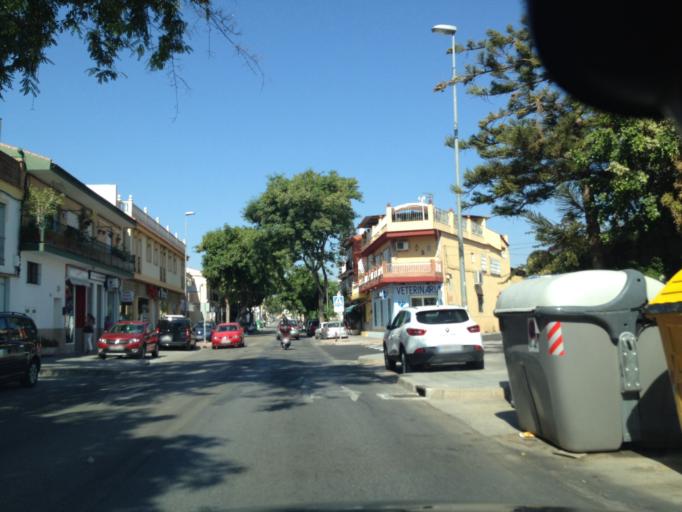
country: ES
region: Andalusia
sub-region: Provincia de Malaga
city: Alhaurin de la Torre
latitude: 36.7246
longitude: -4.5398
